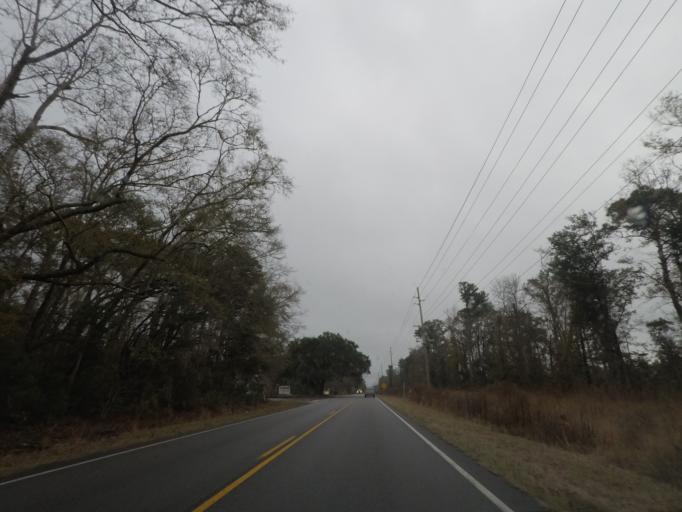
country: US
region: South Carolina
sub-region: Charleston County
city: Meggett
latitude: 32.6763
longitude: -80.3483
